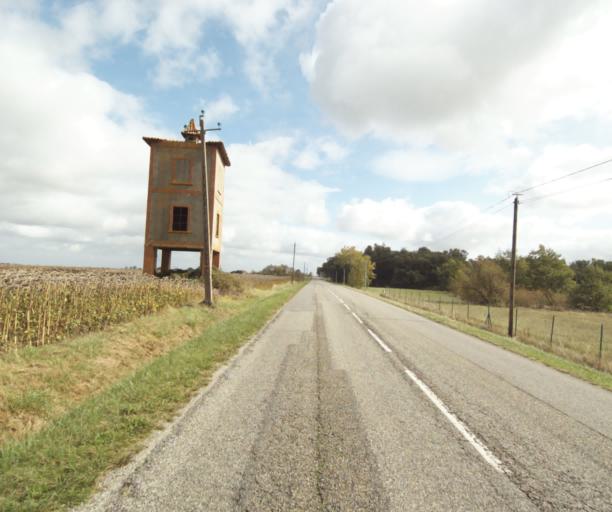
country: FR
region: Midi-Pyrenees
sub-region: Departement du Tarn-et-Garonne
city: Beaumont-de-Lomagne
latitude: 43.8649
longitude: 1.0725
